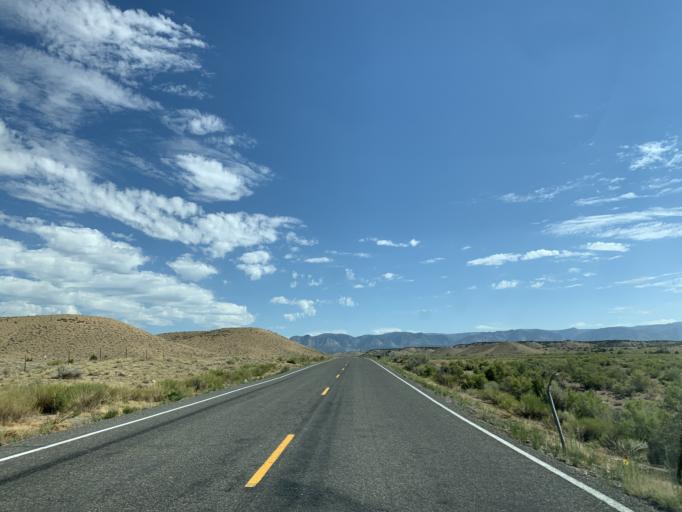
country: US
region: Utah
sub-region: Carbon County
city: Wellington
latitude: 39.5653
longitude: -110.6562
